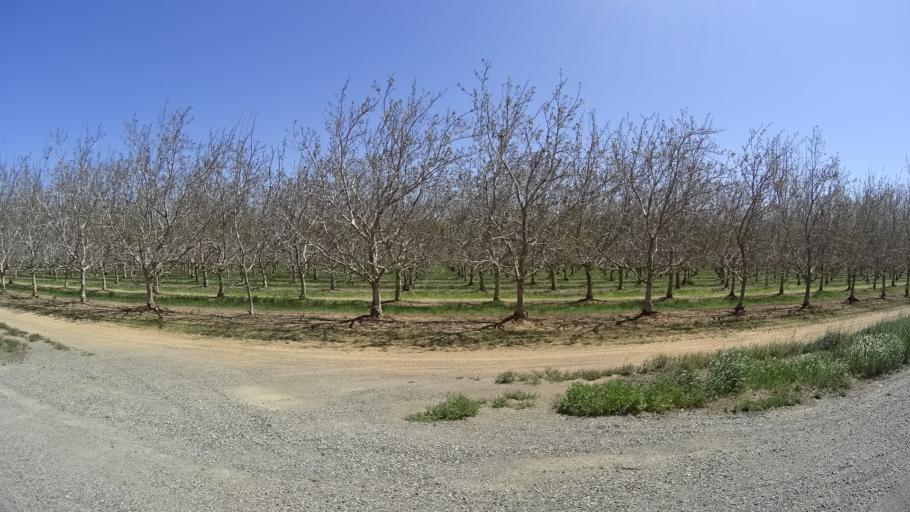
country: US
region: California
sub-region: Glenn County
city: Orland
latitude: 39.7852
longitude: -122.1410
